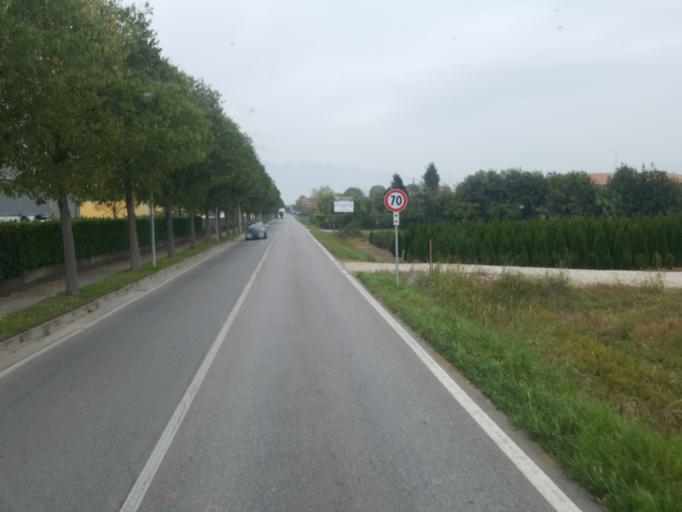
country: IT
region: Veneto
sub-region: Provincia di Treviso
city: Ramon
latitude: 45.7194
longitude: 11.8673
